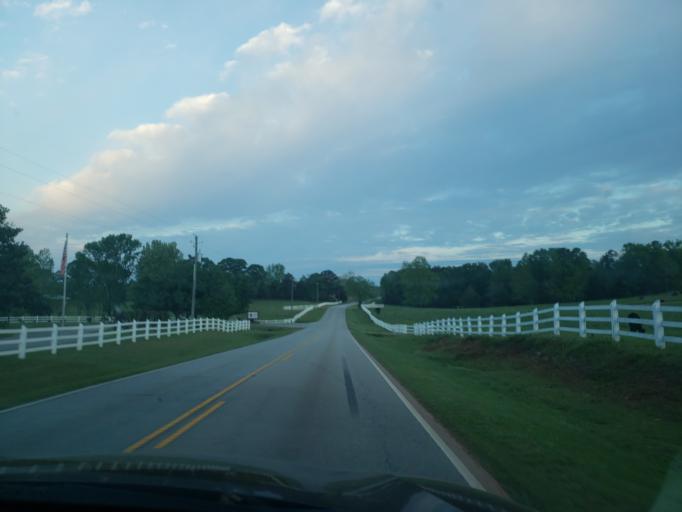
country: US
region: Alabama
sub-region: Tallapoosa County
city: Camp Hill
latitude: 32.6999
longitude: -85.6887
